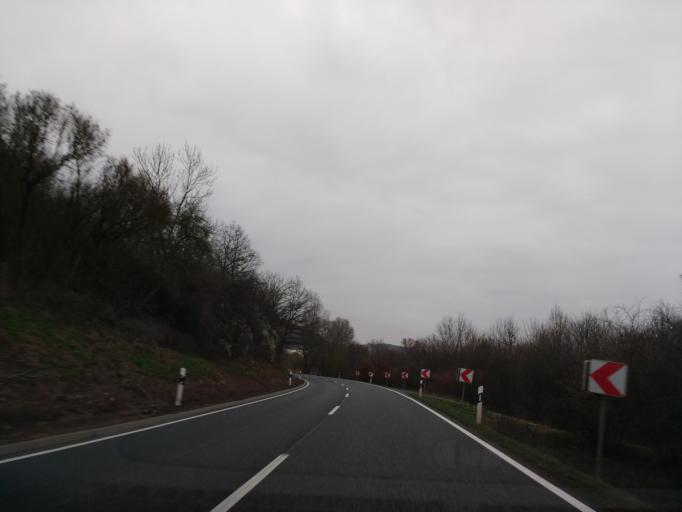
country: DE
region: Hesse
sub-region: Regierungsbezirk Kassel
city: Malsfeld
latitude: 51.0688
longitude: 9.5944
